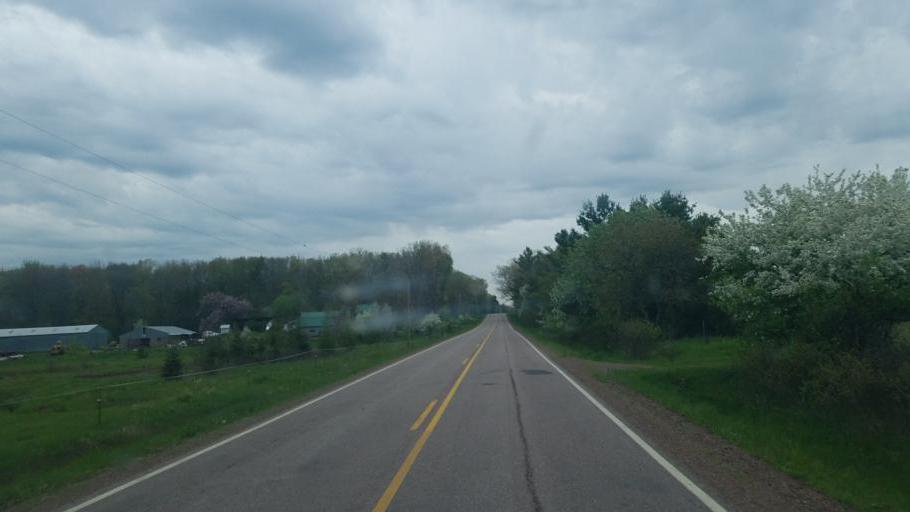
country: US
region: Wisconsin
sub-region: Wood County
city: Marshfield
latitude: 44.4654
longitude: -90.2801
